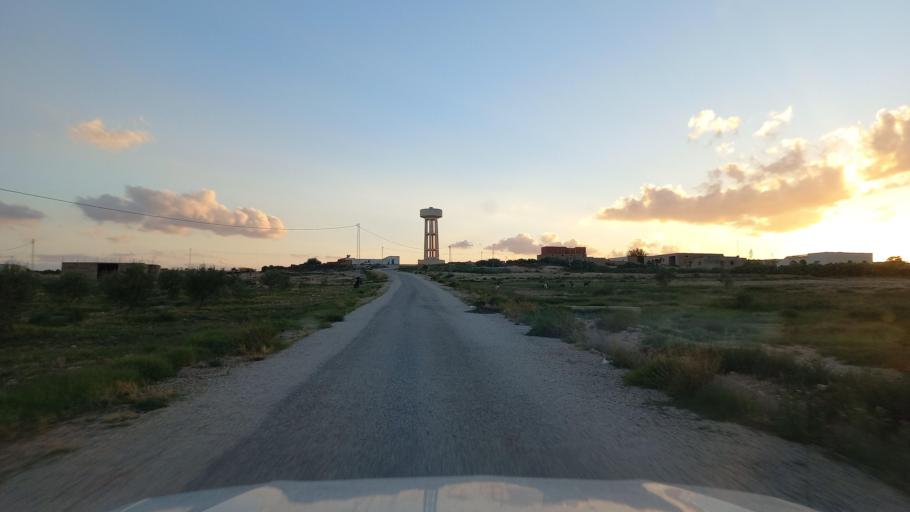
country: TN
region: Al Qasrayn
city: Sbiba
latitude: 35.3738
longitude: 9.0654
